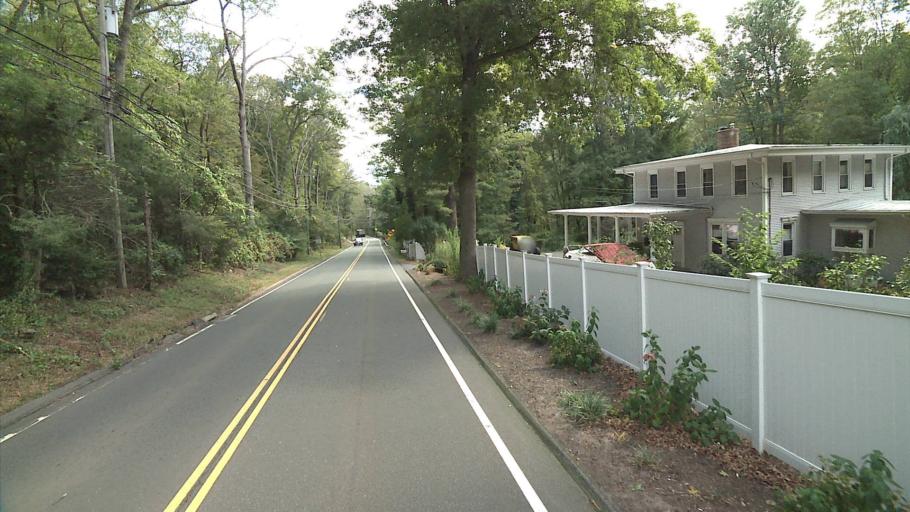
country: US
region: Connecticut
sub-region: Middlesex County
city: Chester Center
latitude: 41.3988
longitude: -72.4688
